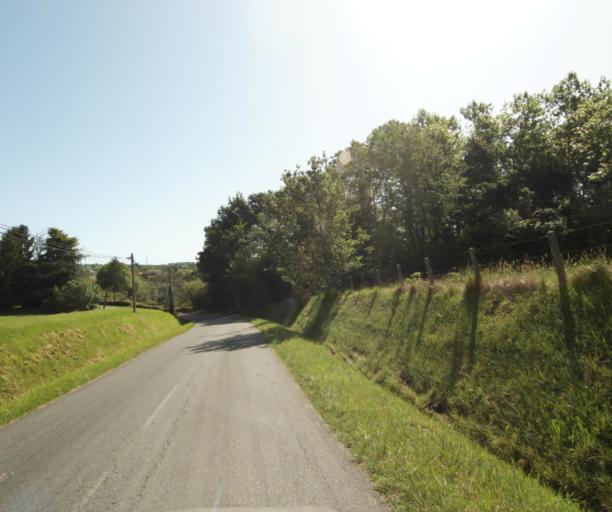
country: FR
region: Aquitaine
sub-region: Departement des Pyrenees-Atlantiques
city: Villefranque
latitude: 43.4620
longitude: -1.4475
